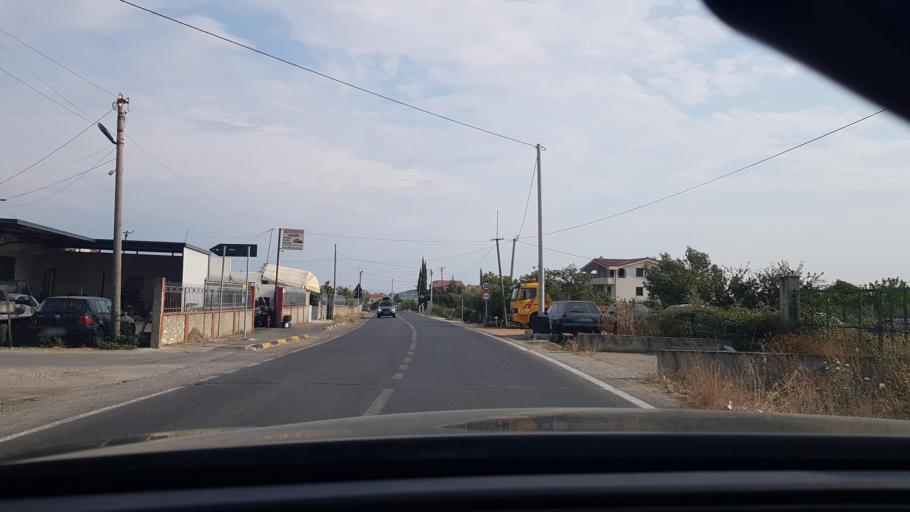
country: AL
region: Durres
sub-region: Rrethi i Durresit
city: Manze
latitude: 41.4660
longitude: 19.5624
